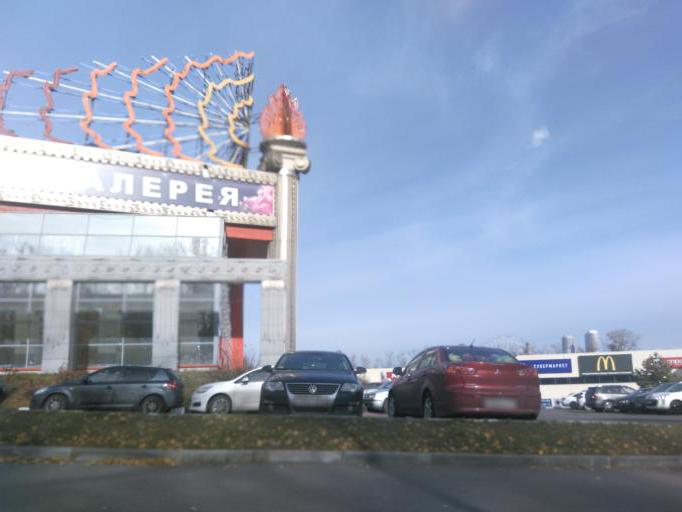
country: RU
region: Moscow
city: Ostankinskiy
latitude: 55.8236
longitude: 37.6328
